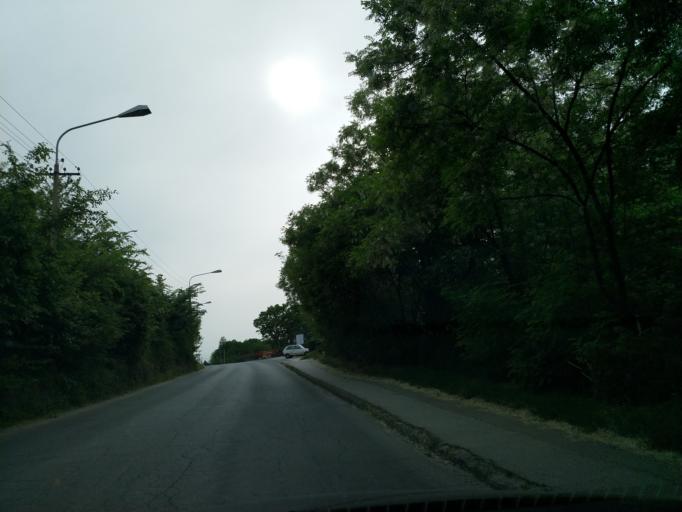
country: RS
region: Central Serbia
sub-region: Pomoravski Okrug
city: Jagodina
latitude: 43.9768
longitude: 21.2474
